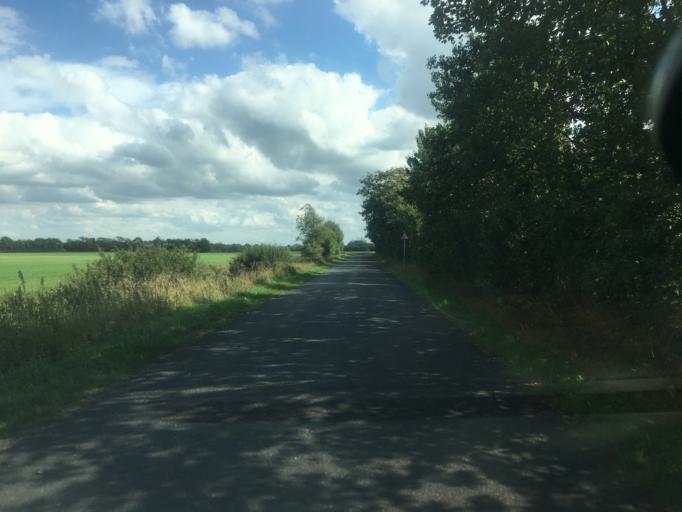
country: DK
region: South Denmark
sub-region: Tonder Kommune
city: Logumkloster
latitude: 55.0062
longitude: 9.0100
